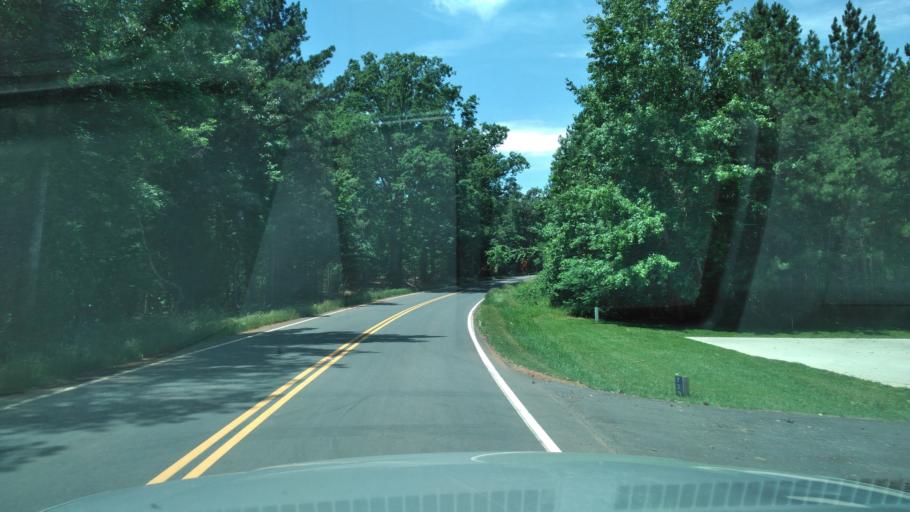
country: US
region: South Carolina
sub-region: Greenwood County
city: Ware Shoals
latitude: 34.4288
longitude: -82.1386
